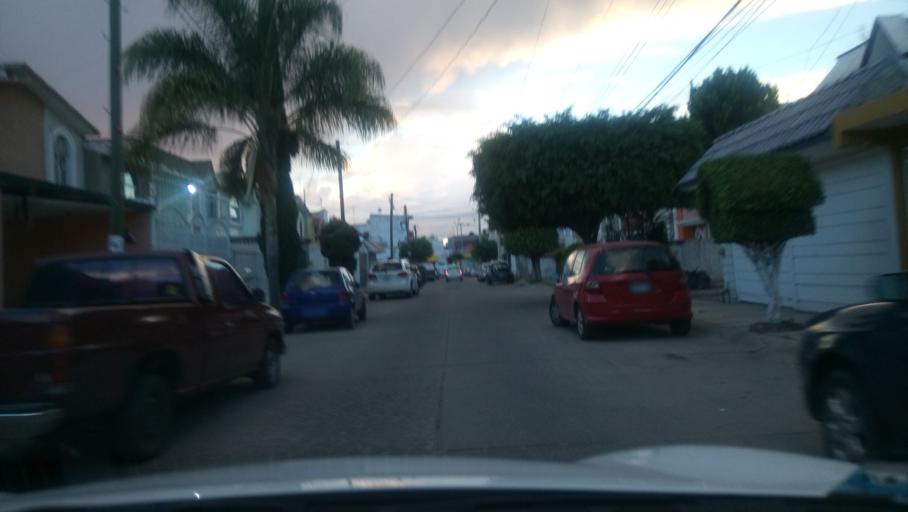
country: MX
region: Guanajuato
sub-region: Leon
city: Medina
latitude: 21.1588
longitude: -101.6491
